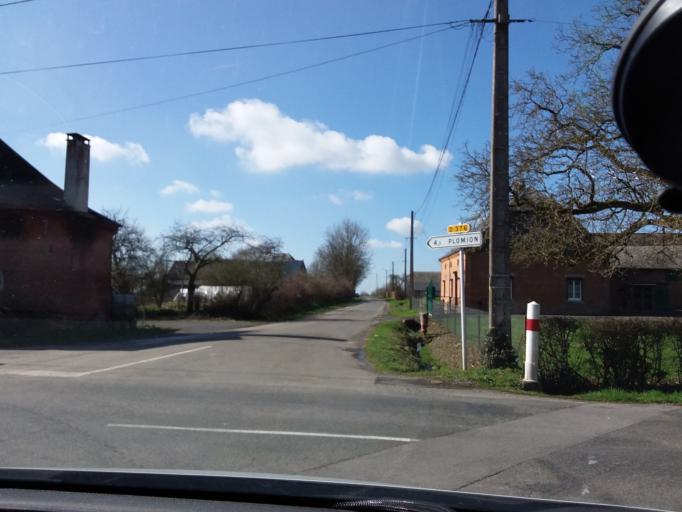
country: FR
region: Picardie
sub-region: Departement de l'Aisne
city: Origny-en-Thierache
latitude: 49.8378
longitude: 4.0616
